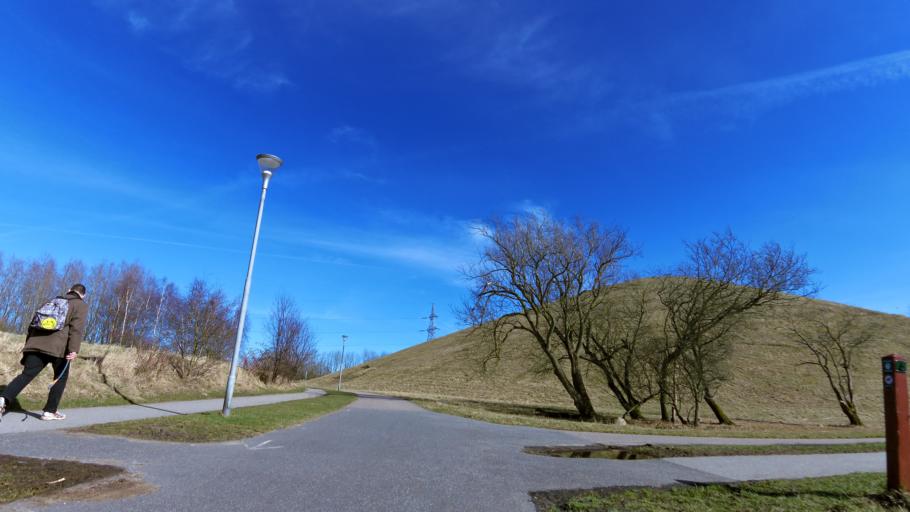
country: DK
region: Central Jutland
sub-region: Arhus Kommune
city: Stavtrup
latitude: 56.1691
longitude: 10.1401
